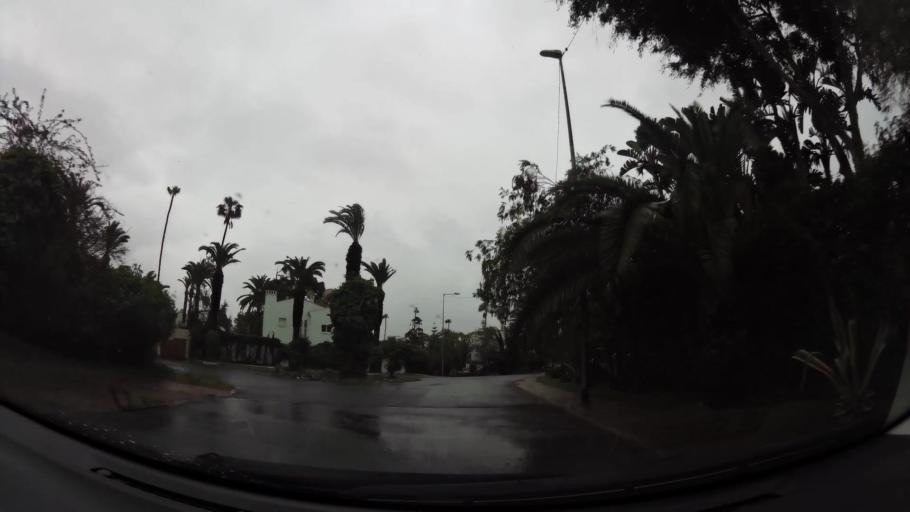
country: MA
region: Grand Casablanca
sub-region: Casablanca
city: Casablanca
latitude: 33.5897
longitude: -7.6612
